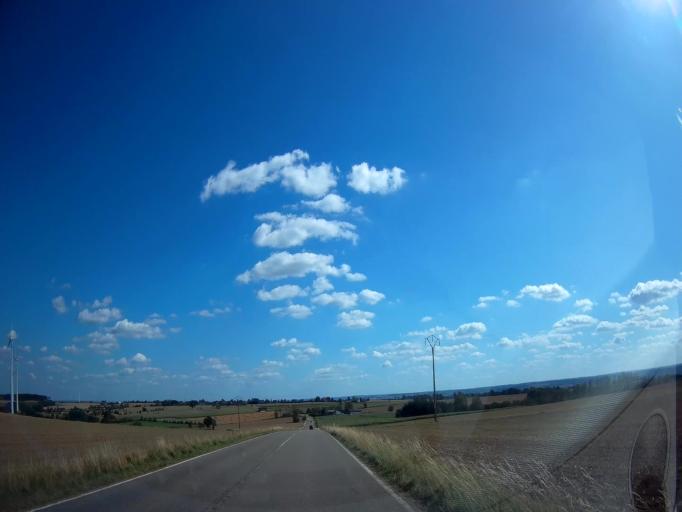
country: FR
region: Champagne-Ardenne
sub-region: Departement des Ardennes
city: Fromelennes
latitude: 50.1776
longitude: 4.8661
